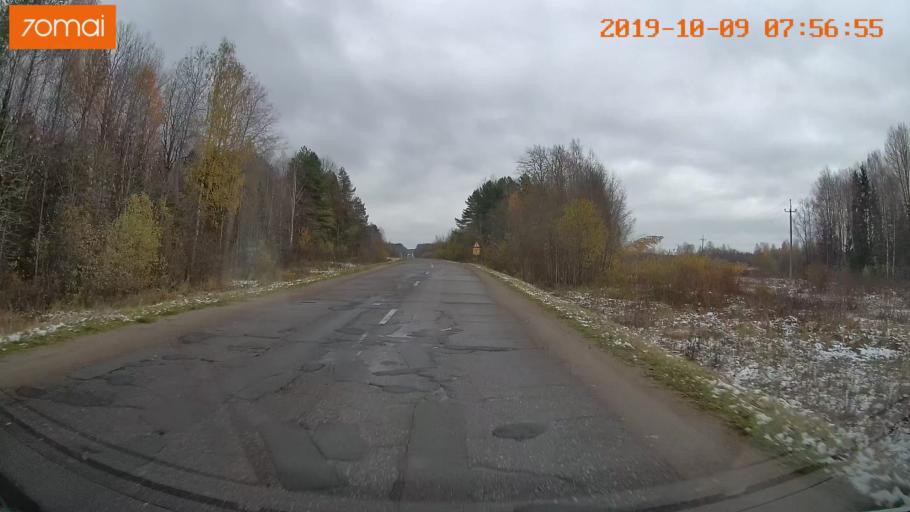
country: RU
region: Jaroslavl
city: Kukoboy
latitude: 58.6971
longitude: 39.9430
